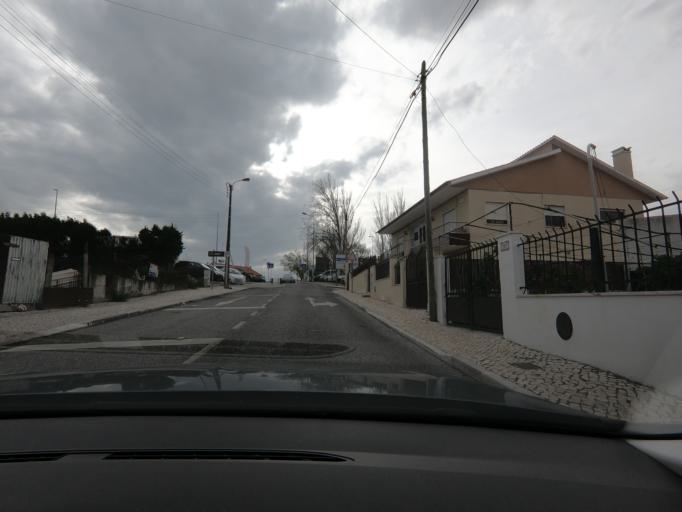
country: PT
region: Lisbon
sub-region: Cascais
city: Sao Domingos de Rana
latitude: 38.7127
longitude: -9.3380
